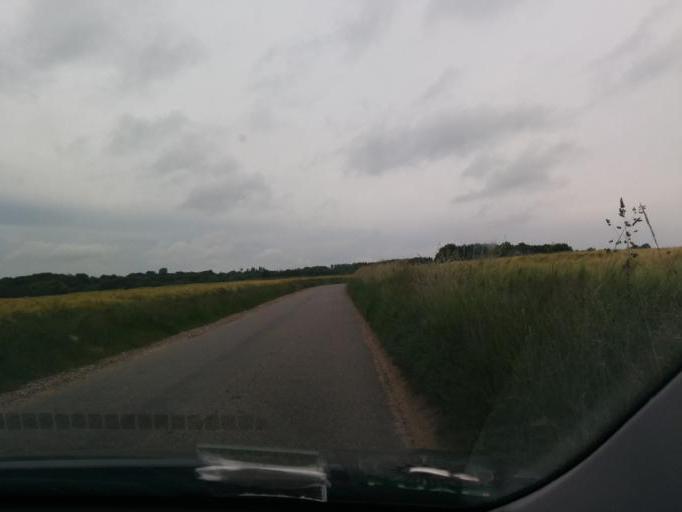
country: DK
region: Central Jutland
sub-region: Syddjurs Kommune
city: Hornslet
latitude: 56.2936
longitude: 10.3862
